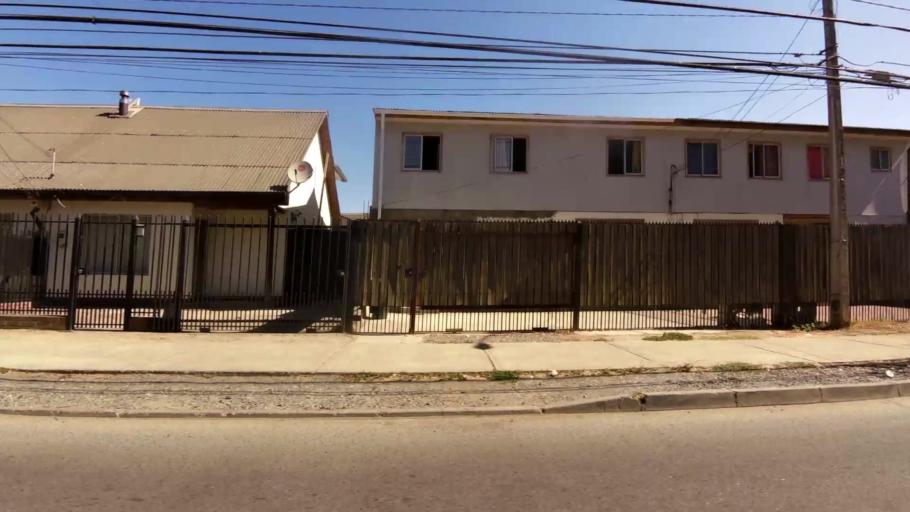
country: CL
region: Maule
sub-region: Provincia de Talca
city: Talca
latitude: -35.4264
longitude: -71.6298
